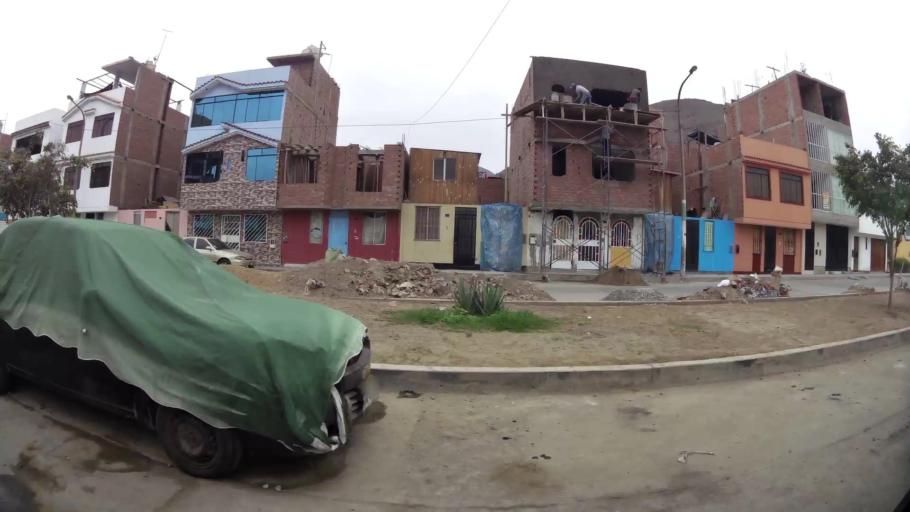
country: PE
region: Lima
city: Ventanilla
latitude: -11.9303
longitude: -77.0814
